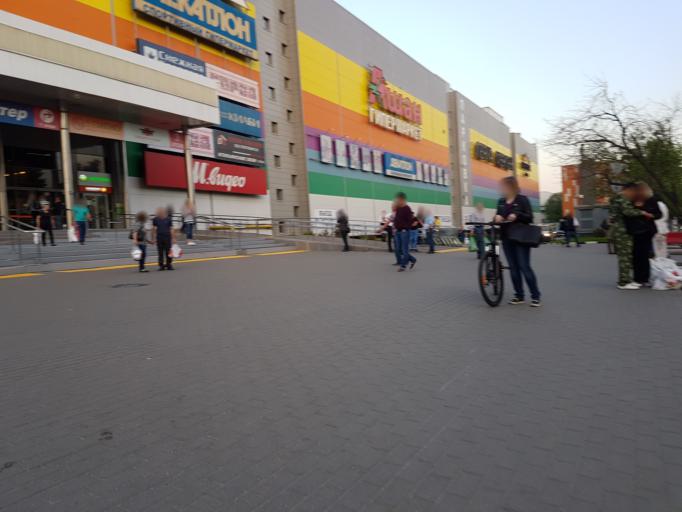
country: RU
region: Moscow
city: Lefortovo
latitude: 55.7480
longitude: 37.7046
